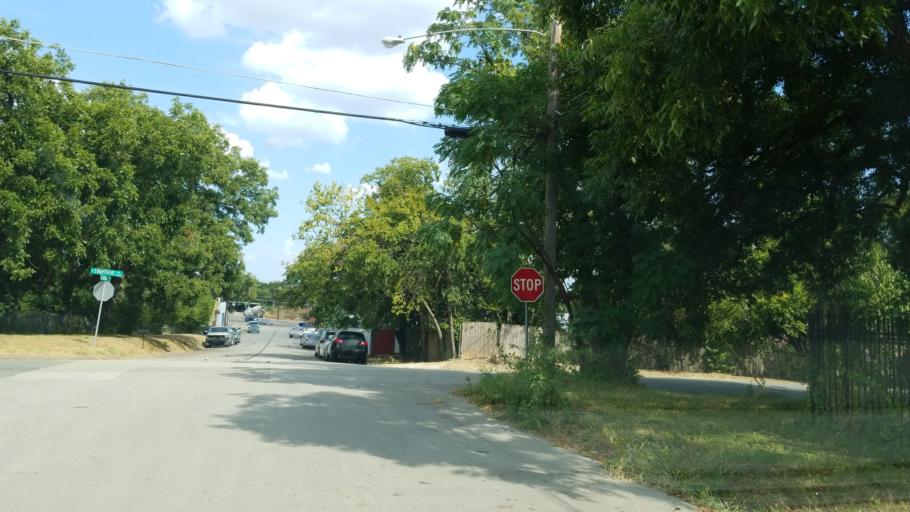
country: US
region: Texas
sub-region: Dallas County
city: Dallas
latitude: 32.7674
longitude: -96.8421
